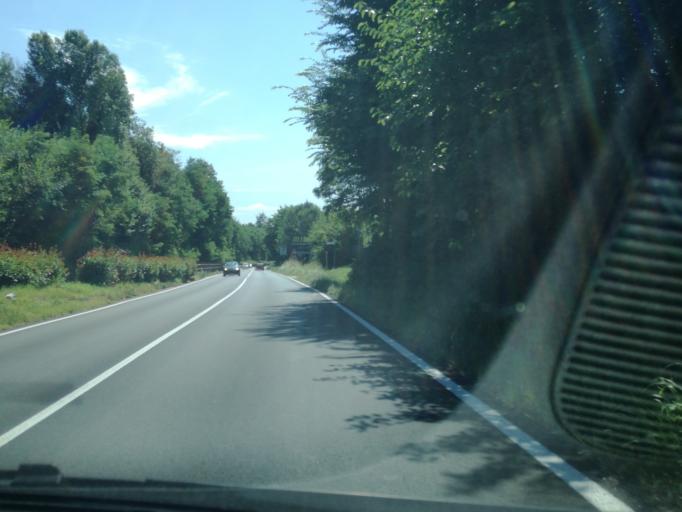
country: IT
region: Lombardy
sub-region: Provincia di Bergamo
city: Terno d'Isola
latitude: 45.6903
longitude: 9.5218
